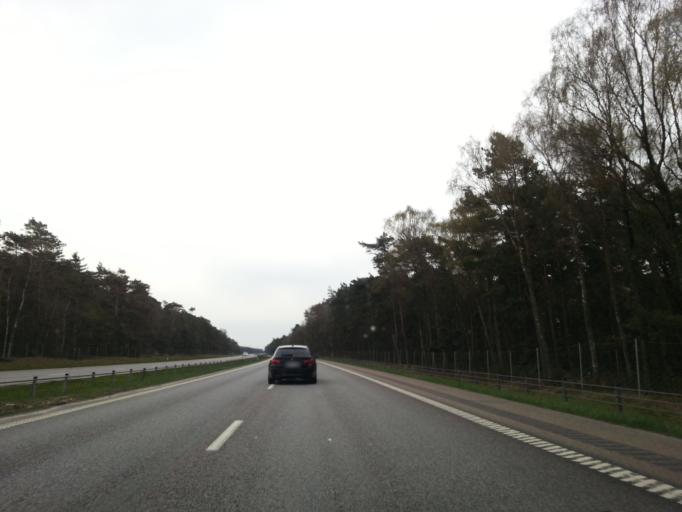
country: SE
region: Halland
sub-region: Halmstads Kommun
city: Paarp
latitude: 56.5655
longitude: 12.9516
